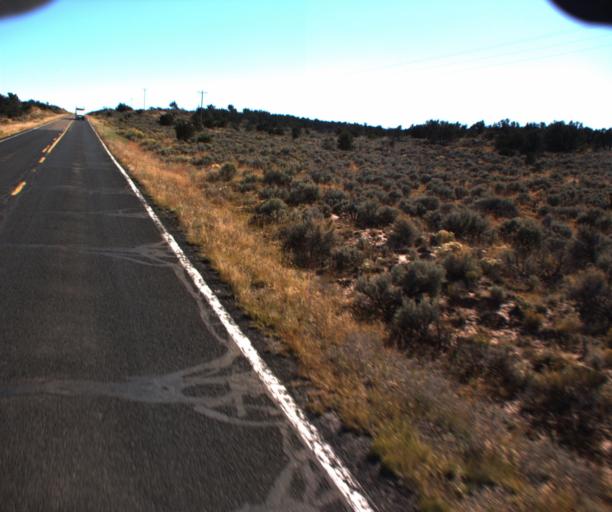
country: US
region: Arizona
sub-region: Apache County
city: Ganado
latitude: 35.5960
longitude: -109.5388
